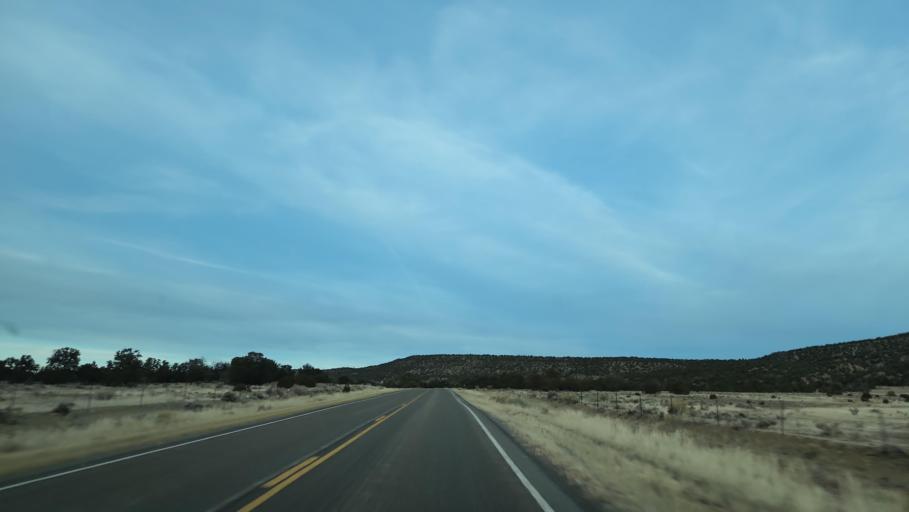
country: US
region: New Mexico
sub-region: Cibola County
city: Grants
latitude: 34.7313
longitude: -107.9682
